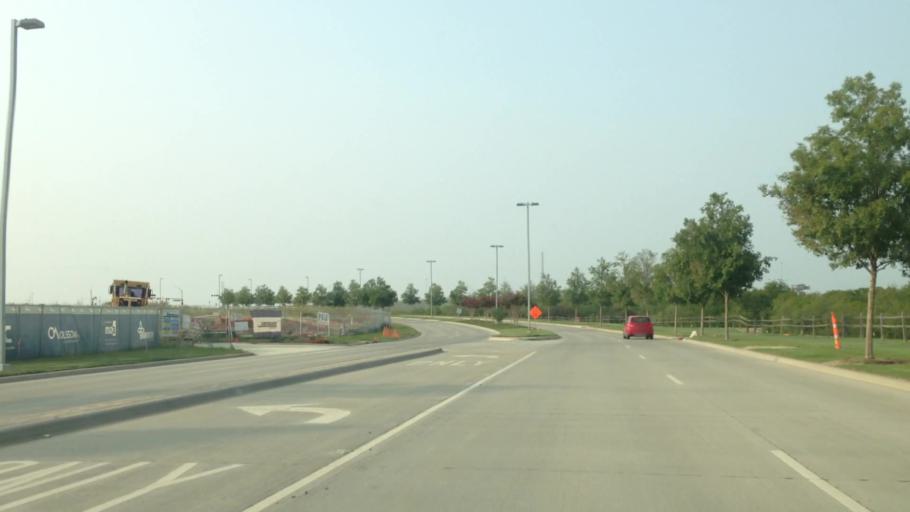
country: US
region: Texas
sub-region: Denton County
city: The Colony
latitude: 33.0744
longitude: -96.8565
